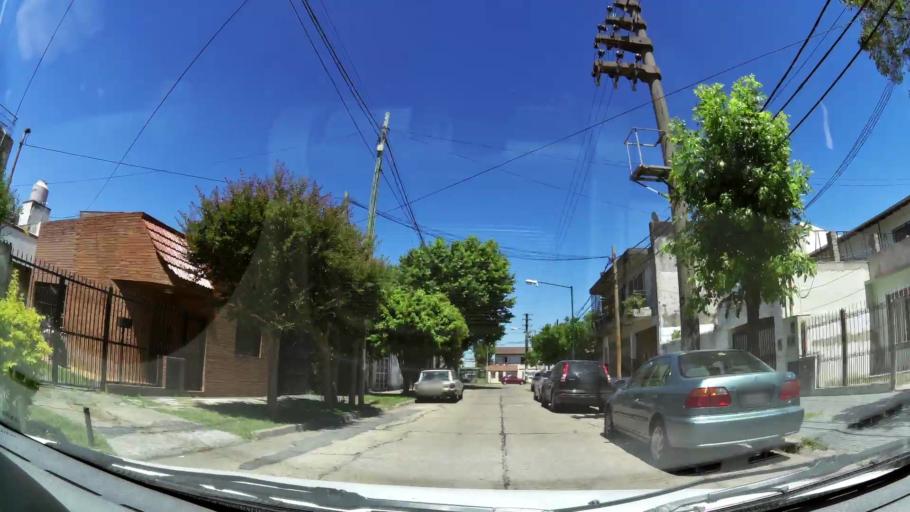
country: AR
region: Buenos Aires
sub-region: Partido de San Isidro
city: San Isidro
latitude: -34.5106
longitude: -58.5591
